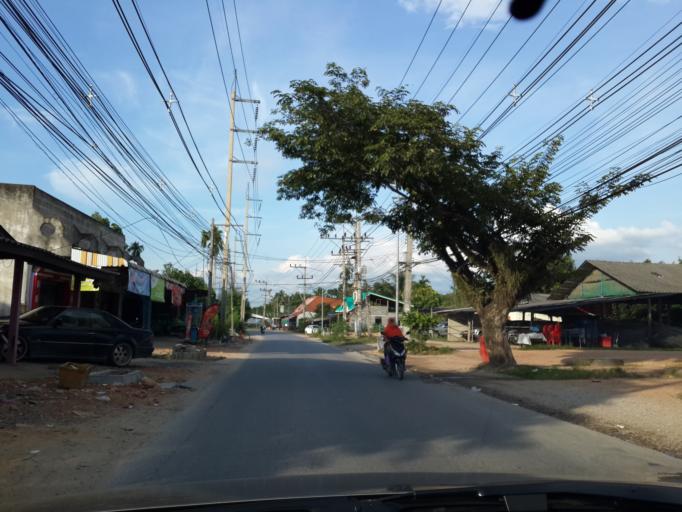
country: TH
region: Yala
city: Yala
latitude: 6.5037
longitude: 101.2688
